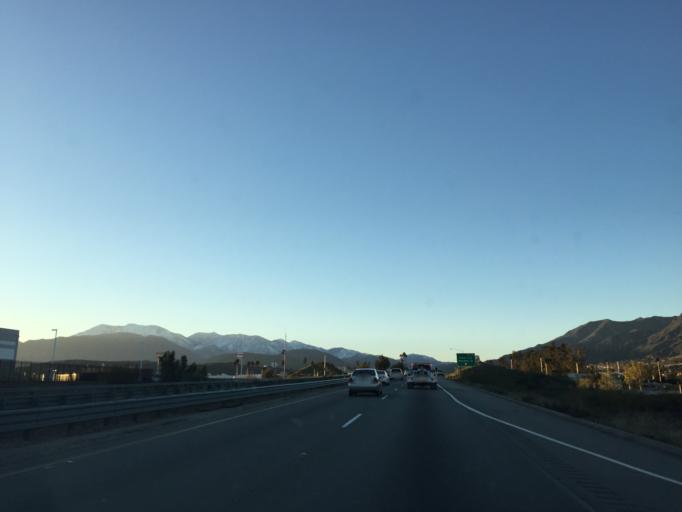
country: US
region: California
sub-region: San Bernardino County
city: Muscoy
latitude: 34.1884
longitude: -117.3574
